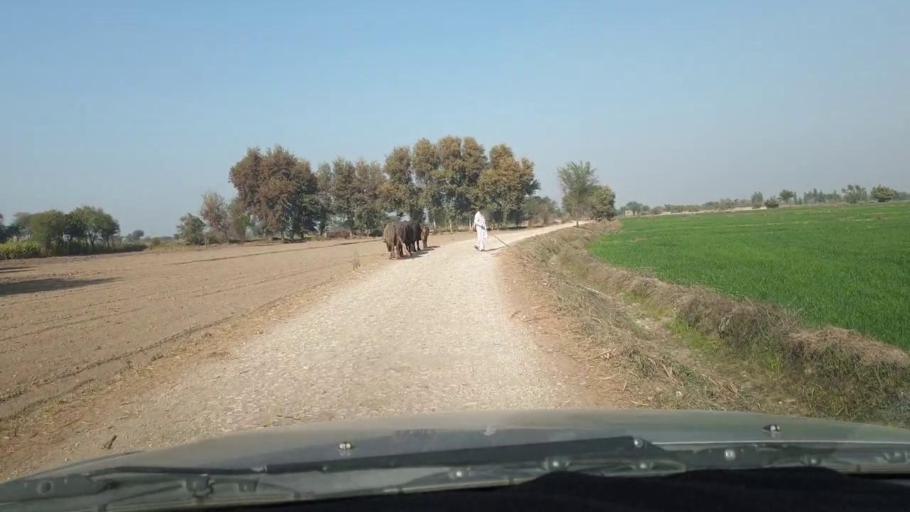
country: PK
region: Sindh
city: Mirpur Mathelo
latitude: 27.9242
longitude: 69.5605
